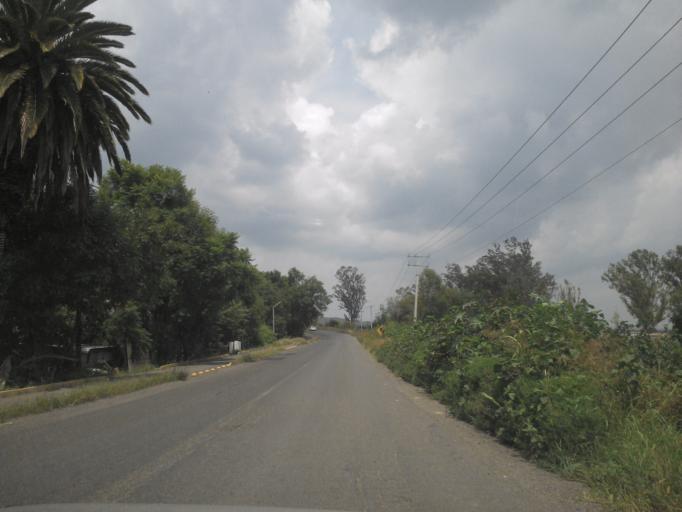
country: MX
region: Jalisco
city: San Diego de Alejandria
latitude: 20.8856
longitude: -101.9742
